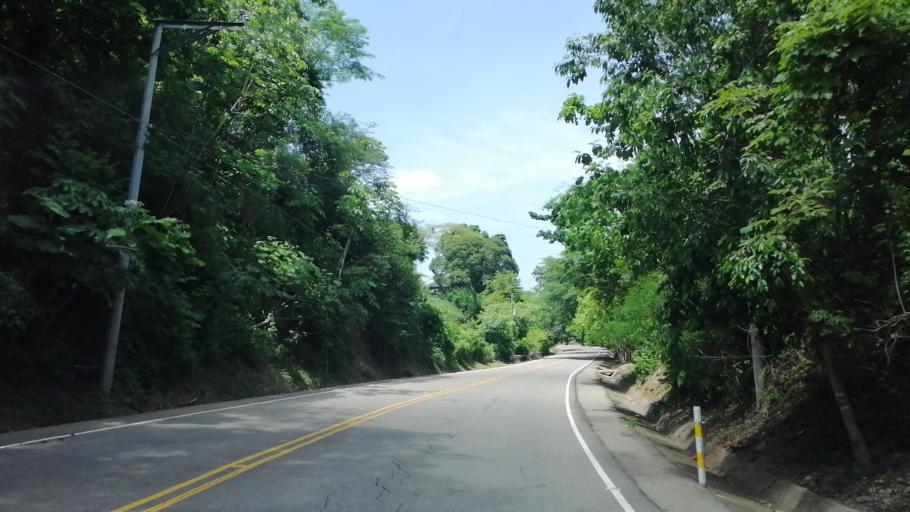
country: SV
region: Chalatenango
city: Nueva Concepcion
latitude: 14.1805
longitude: -89.3215
